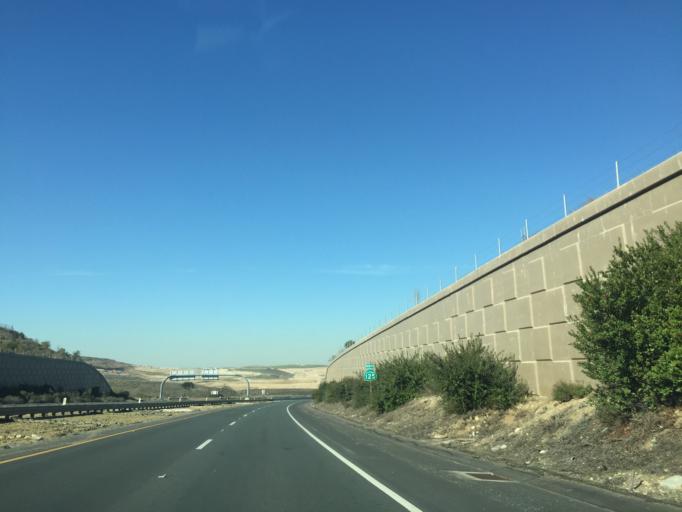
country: MX
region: Baja California
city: Tijuana
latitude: 32.5827
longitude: -116.9639
